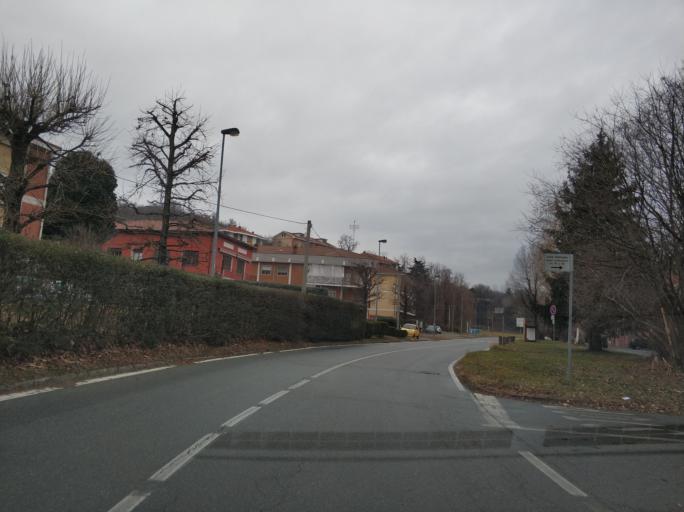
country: IT
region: Piedmont
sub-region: Provincia di Torino
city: Pavone Canavese
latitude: 45.4414
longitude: 7.8651
